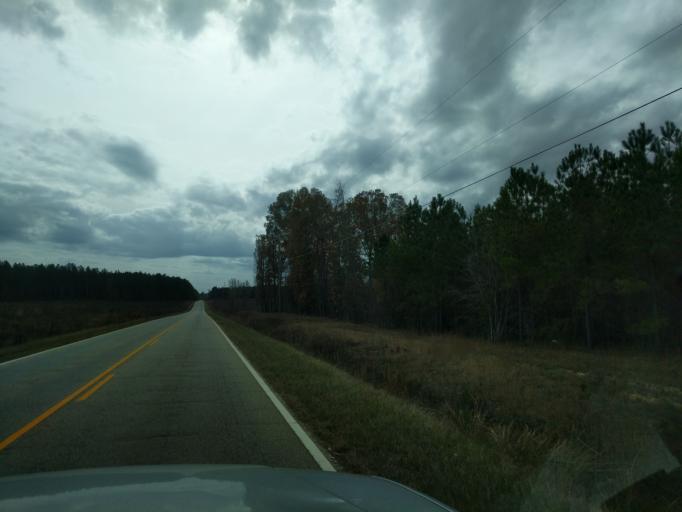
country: US
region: South Carolina
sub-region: Saluda County
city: Saluda
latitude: 34.1073
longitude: -81.8303
